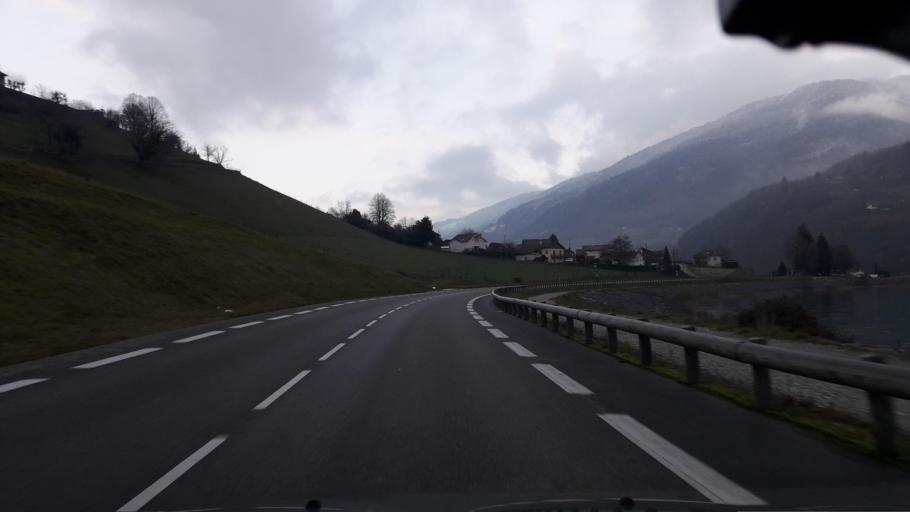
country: FR
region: Rhone-Alpes
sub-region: Departement de l'Isere
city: Allevard
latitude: 45.3842
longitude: 6.0572
